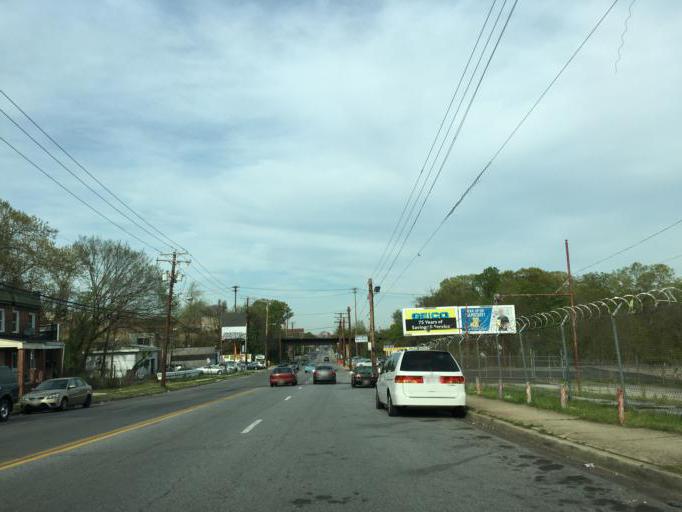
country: US
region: Maryland
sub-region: Baltimore County
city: Lansdowne
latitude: 39.2753
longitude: -76.6668
